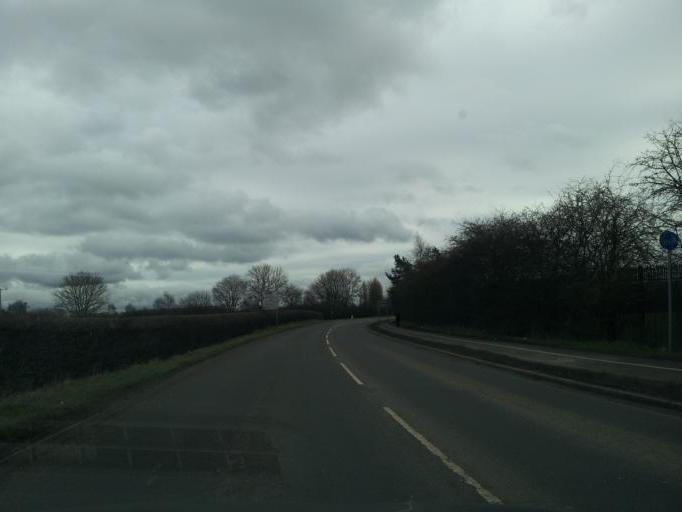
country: GB
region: England
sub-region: Staffordshire
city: Stafford
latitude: 52.8301
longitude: -2.1074
